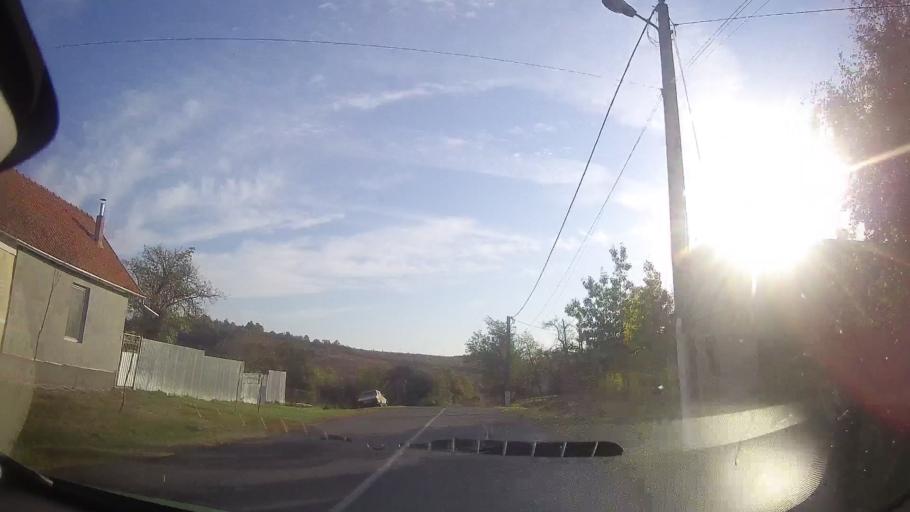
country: RO
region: Timis
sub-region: Comuna Bogda
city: Bogda
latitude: 45.9820
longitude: 21.5547
